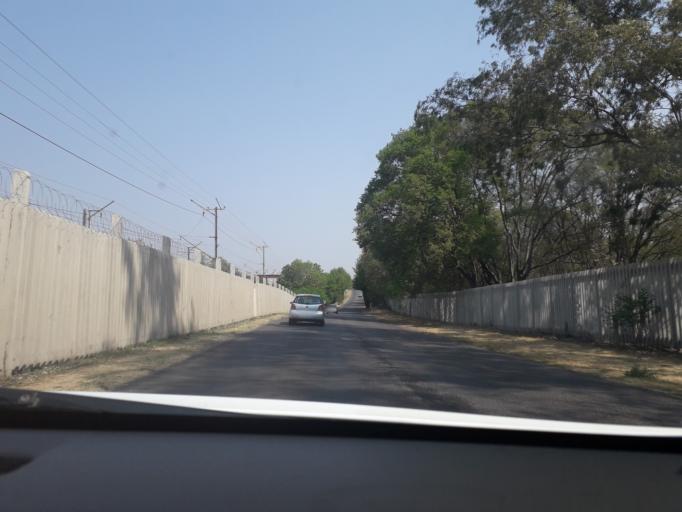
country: ZA
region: Gauteng
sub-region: City of Tshwane Metropolitan Municipality
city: Centurion
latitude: -25.8880
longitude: 28.2242
